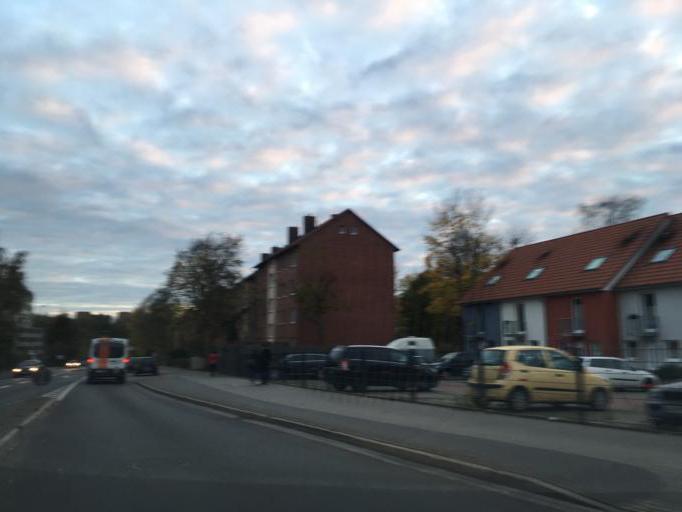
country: DE
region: Lower Saxony
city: Lueneburg
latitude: 53.2474
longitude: 10.4328
